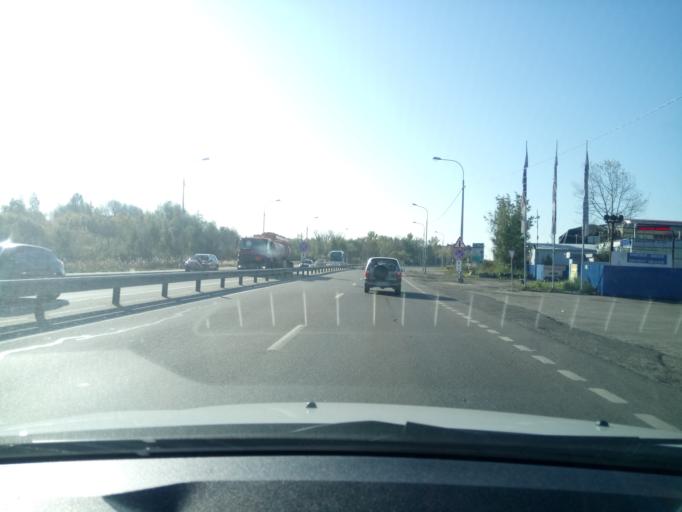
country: RU
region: Nizjnij Novgorod
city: Burevestnik
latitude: 56.1680
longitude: 43.9157
